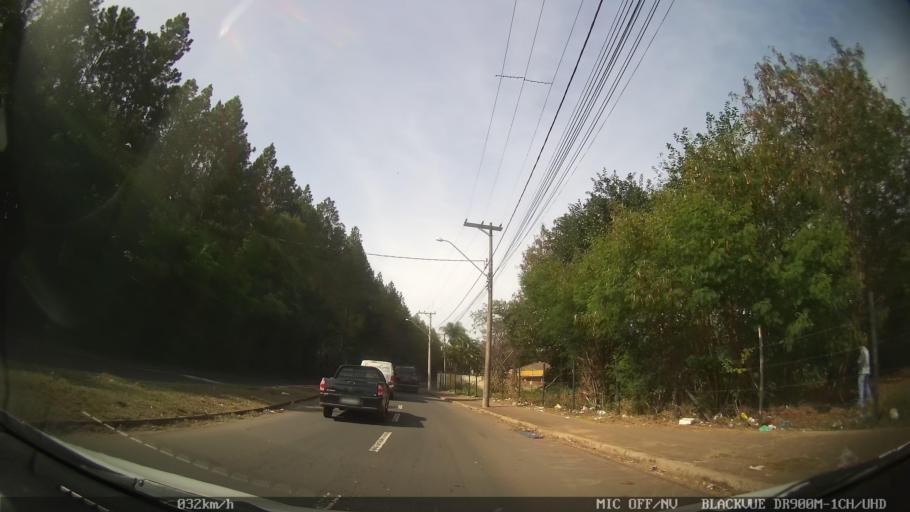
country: BR
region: Sao Paulo
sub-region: Piracicaba
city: Piracicaba
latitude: -22.7566
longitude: -47.6063
